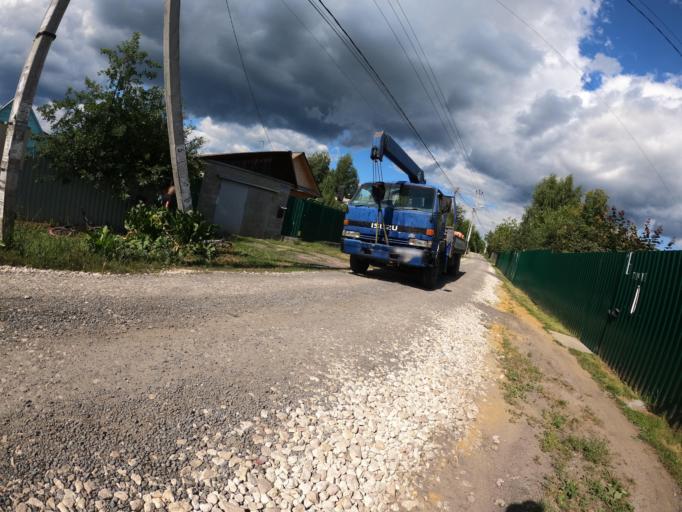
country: RU
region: Moskovskaya
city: Konobeyevo
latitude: 55.4097
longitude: 38.6587
